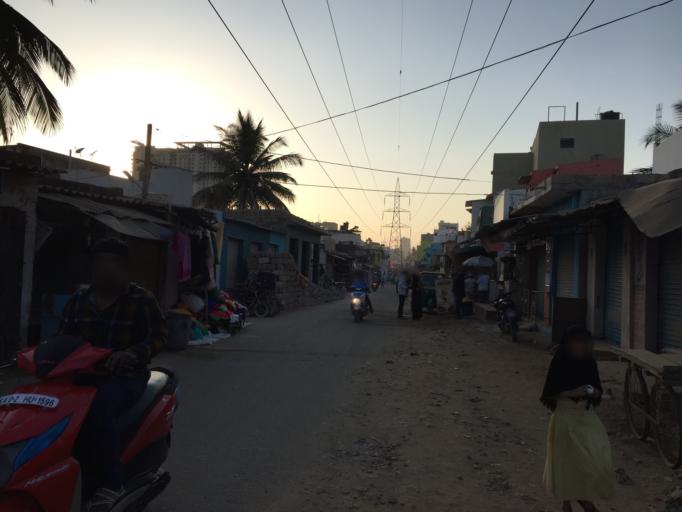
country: IN
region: Karnataka
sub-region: Bangalore Urban
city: Yelahanka
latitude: 13.0506
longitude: 77.6299
